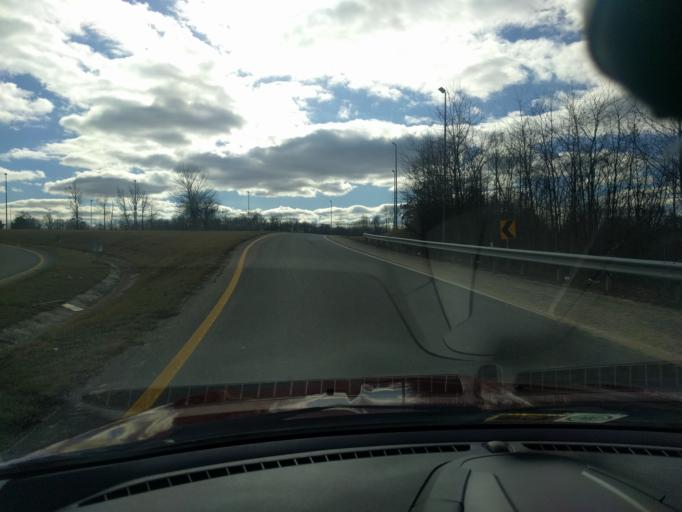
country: US
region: Virginia
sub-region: City of Lynchburg
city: West Lynchburg
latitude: 37.3416
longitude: -79.1939
